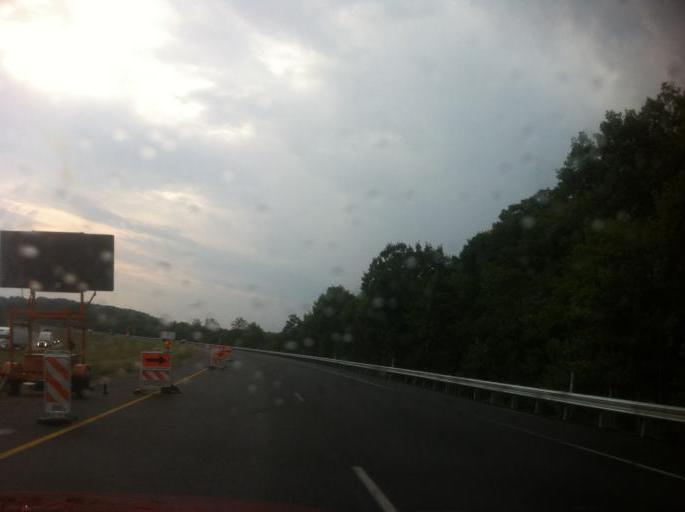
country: US
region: Pennsylvania
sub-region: Clarion County
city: Knox
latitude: 41.1991
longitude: -79.4845
